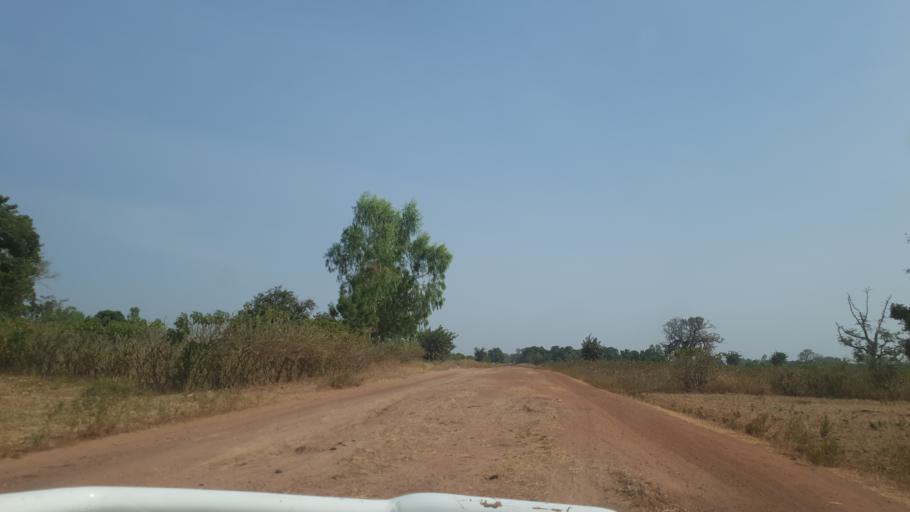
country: ML
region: Koulikoro
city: Dioila
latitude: 12.2239
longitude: -6.2135
